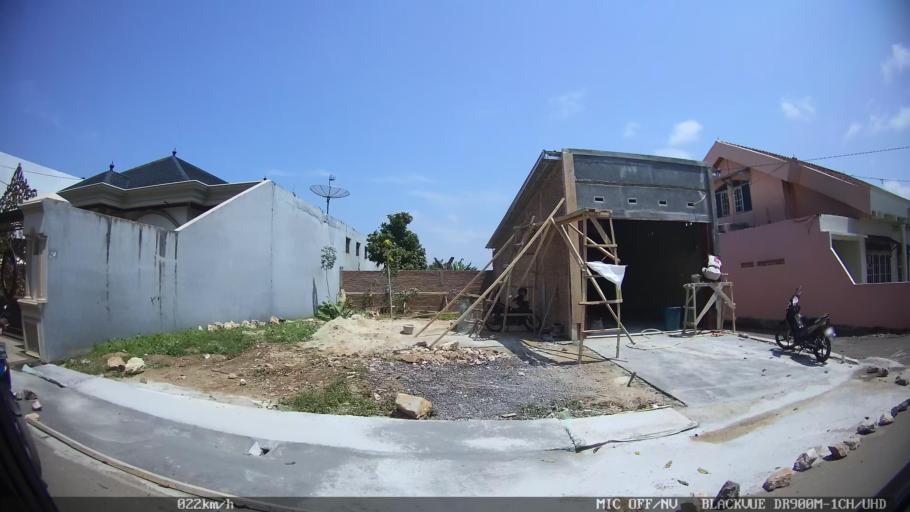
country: ID
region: Lampung
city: Kedaton
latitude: -5.3585
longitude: 105.2759
